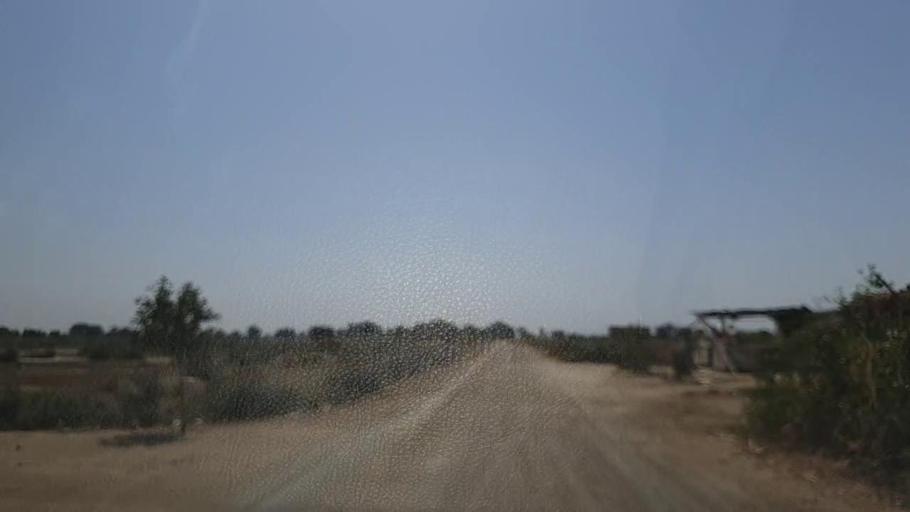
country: PK
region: Sindh
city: Samaro
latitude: 25.2193
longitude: 69.4043
